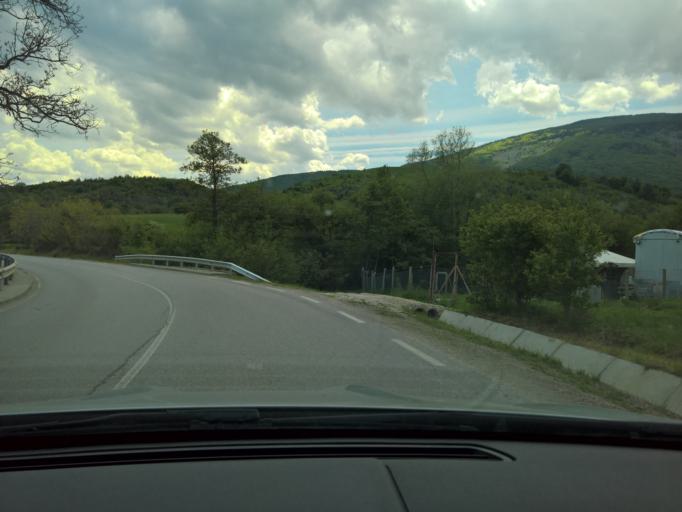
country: BG
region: Sofia-Capital
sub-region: Stolichna Obshtina
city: Sofia
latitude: 42.5729
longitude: 23.3588
